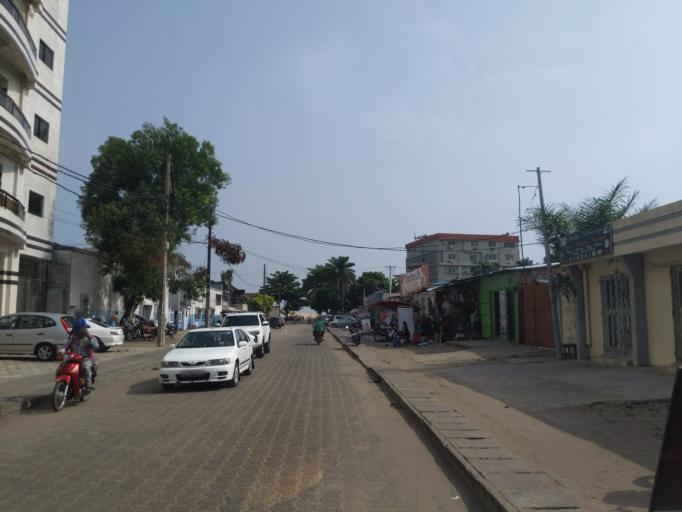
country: BJ
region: Littoral
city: Cotonou
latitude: 6.3602
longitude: 2.4450
